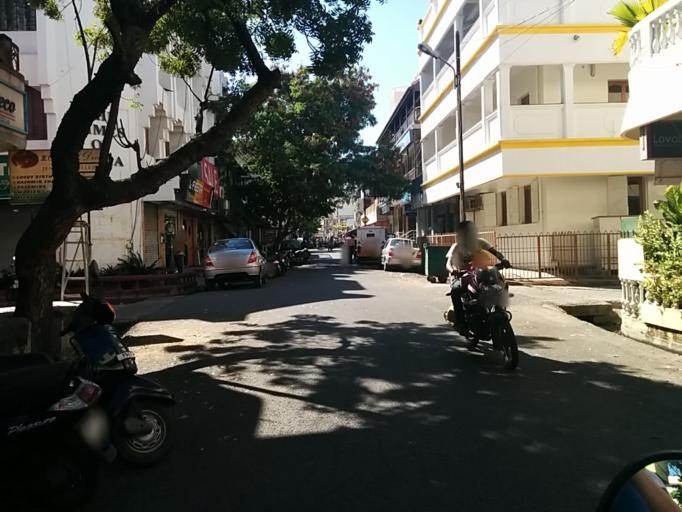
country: IN
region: Pondicherry
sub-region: Puducherry
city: Puducherry
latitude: 11.9364
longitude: 79.8320
